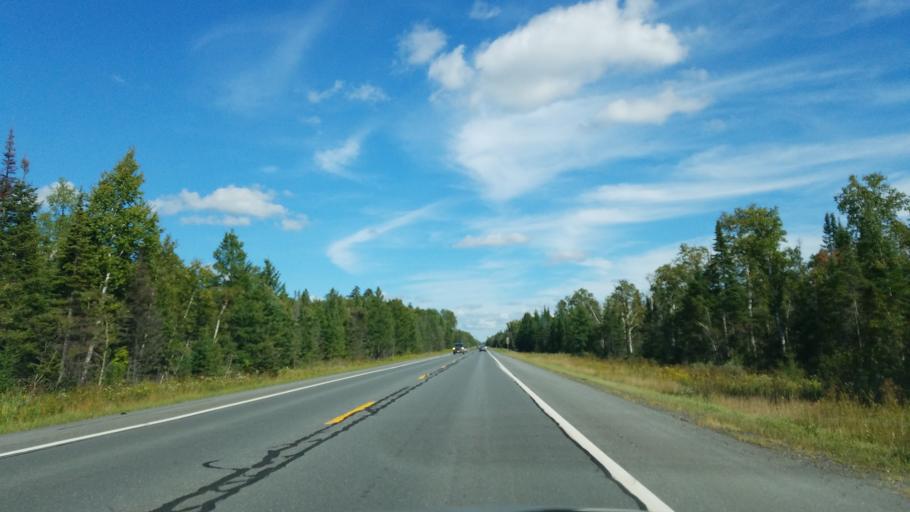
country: US
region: Michigan
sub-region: Baraga County
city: L'Anse
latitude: 46.5788
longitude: -88.4442
